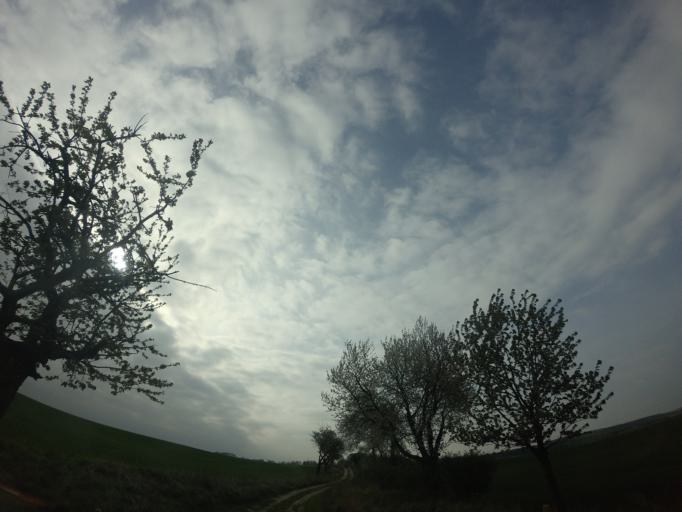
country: PL
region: West Pomeranian Voivodeship
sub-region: Powiat choszczenski
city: Pelczyce
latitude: 53.0732
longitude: 15.2393
